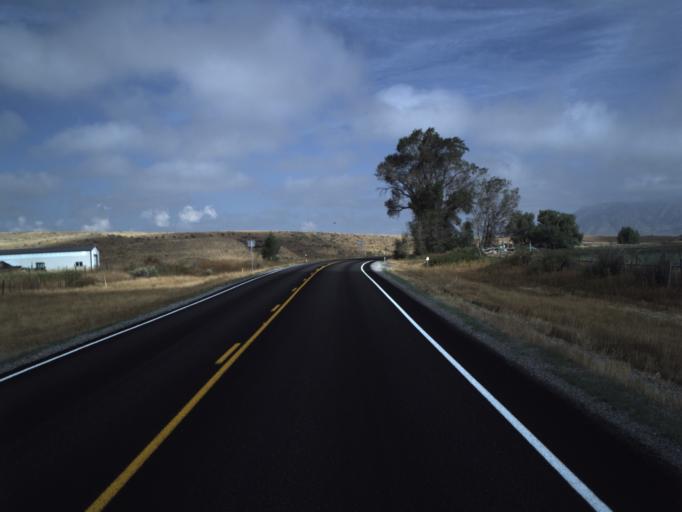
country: US
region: Utah
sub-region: Rich County
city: Randolph
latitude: 41.5346
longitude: -111.1628
